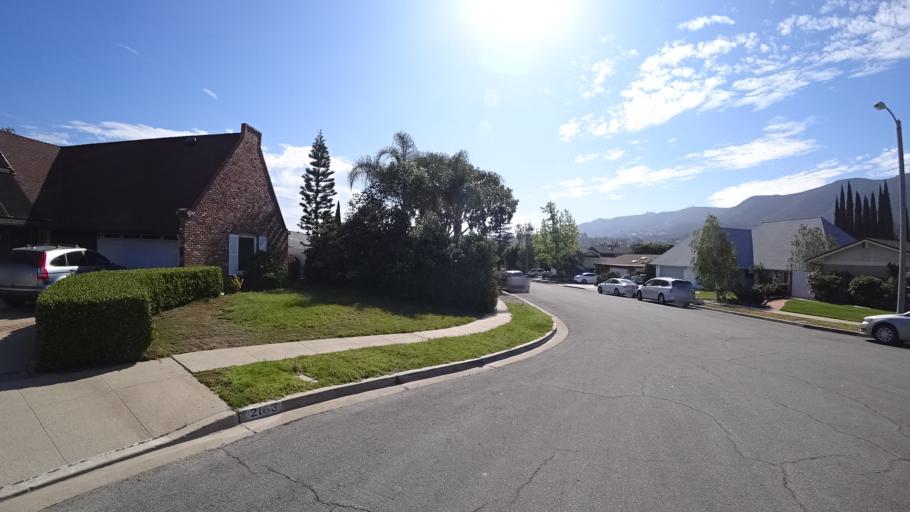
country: US
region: California
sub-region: Ventura County
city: Casa Conejo
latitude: 34.1772
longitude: -118.9250
